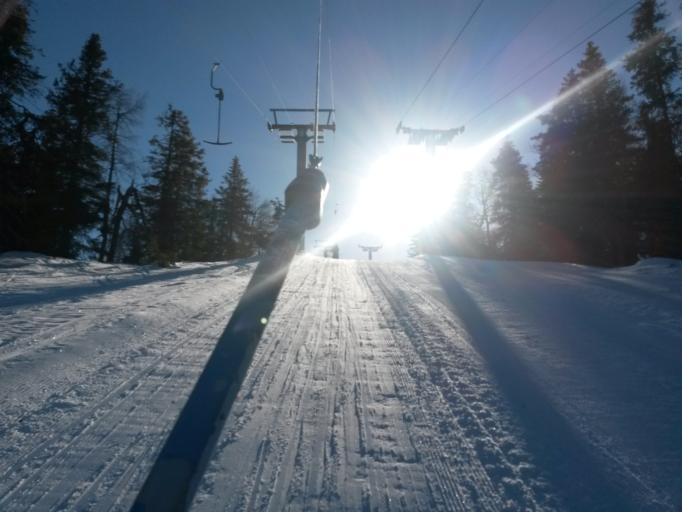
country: SE
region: Vaesterbotten
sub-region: Skelleftea Kommun
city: Langsele
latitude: 65.1550
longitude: 20.1352
